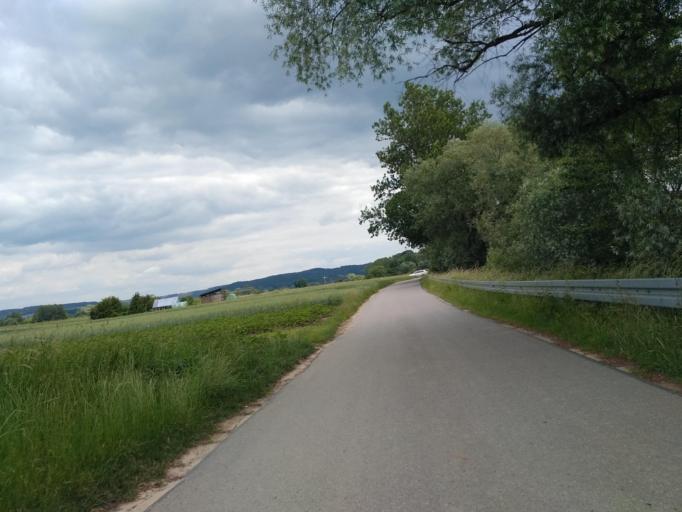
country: PL
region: Subcarpathian Voivodeship
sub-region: Powiat rzeszowski
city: Dynow
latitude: 49.8093
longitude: 22.2439
